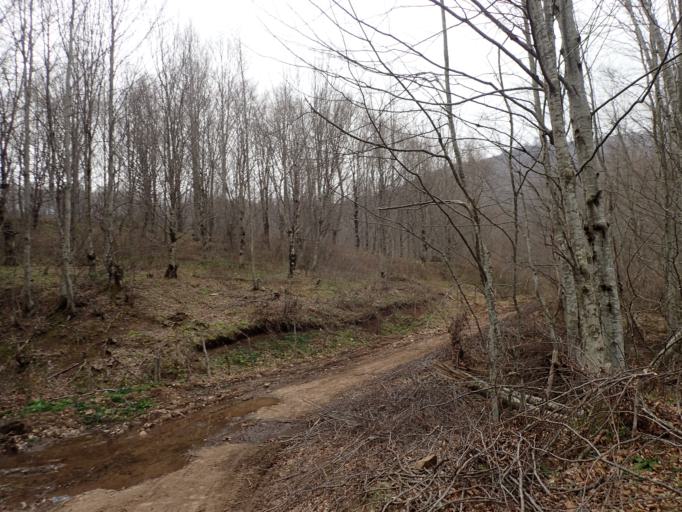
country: TR
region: Ordu
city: Kumru
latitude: 40.7869
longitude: 37.1975
